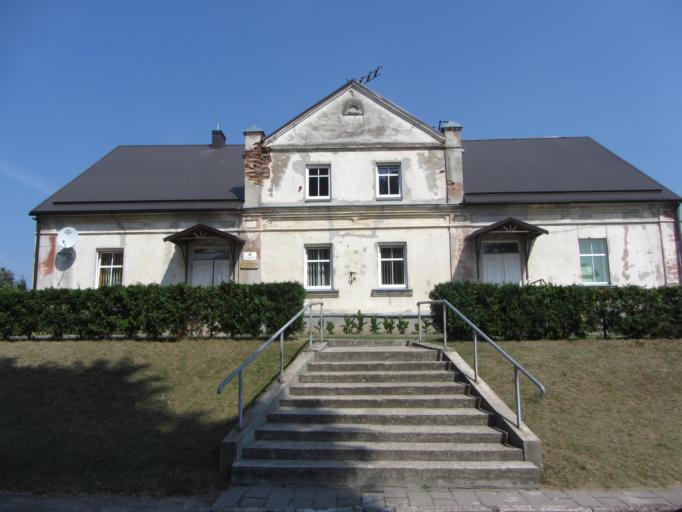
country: LT
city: Veisiejai
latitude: 54.1020
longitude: 23.6953
